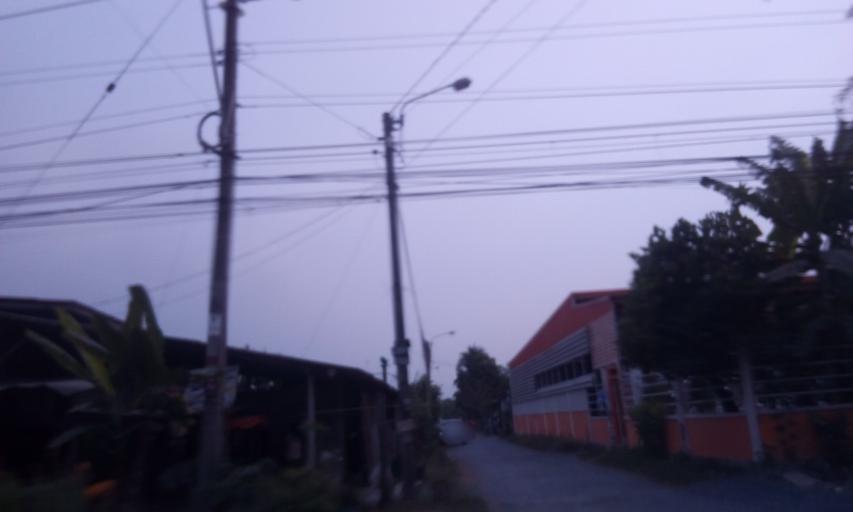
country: TH
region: Bangkok
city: Nong Chok
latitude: 13.8492
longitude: 100.8881
